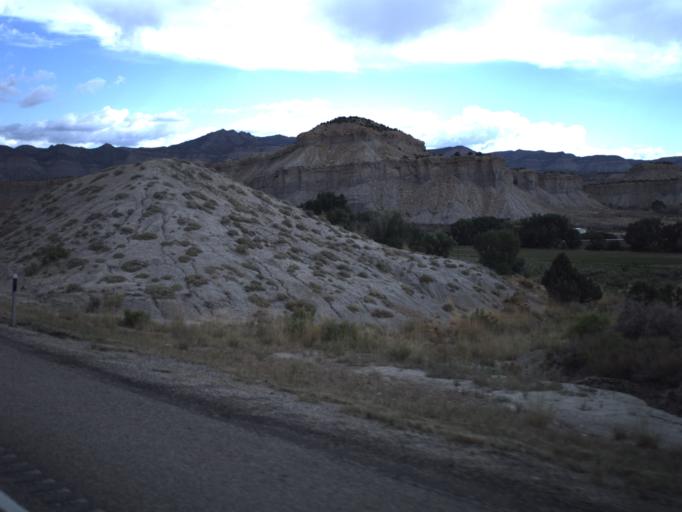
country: US
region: Utah
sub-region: Carbon County
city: Spring Glen
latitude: 39.6316
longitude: -110.8618
